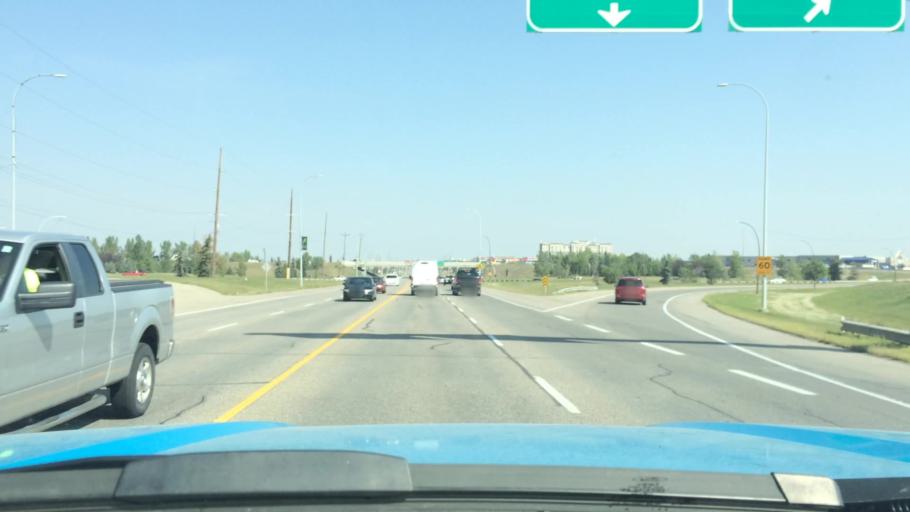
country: CA
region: Alberta
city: Calgary
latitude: 51.0633
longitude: -114.0016
